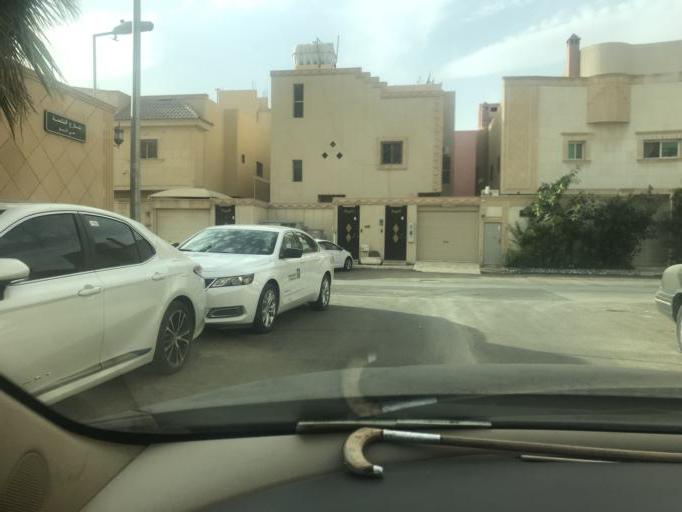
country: SA
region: Ar Riyad
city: Riyadh
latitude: 24.8000
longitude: 46.6694
